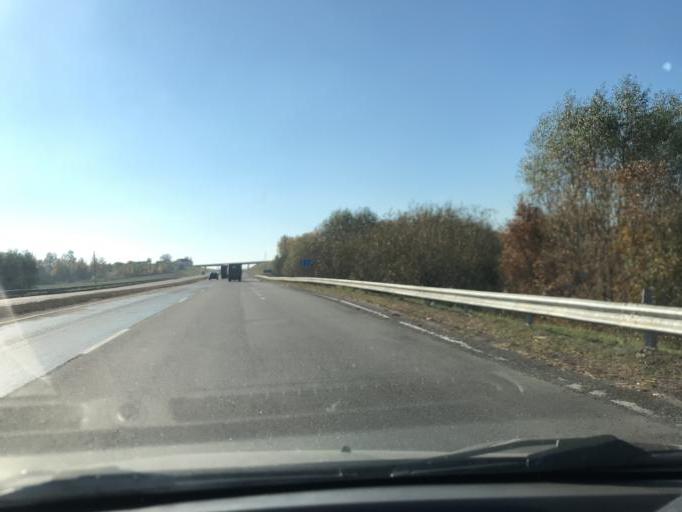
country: BY
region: Gomel
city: Horad Rechytsa
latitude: 52.3025
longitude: 30.4903
